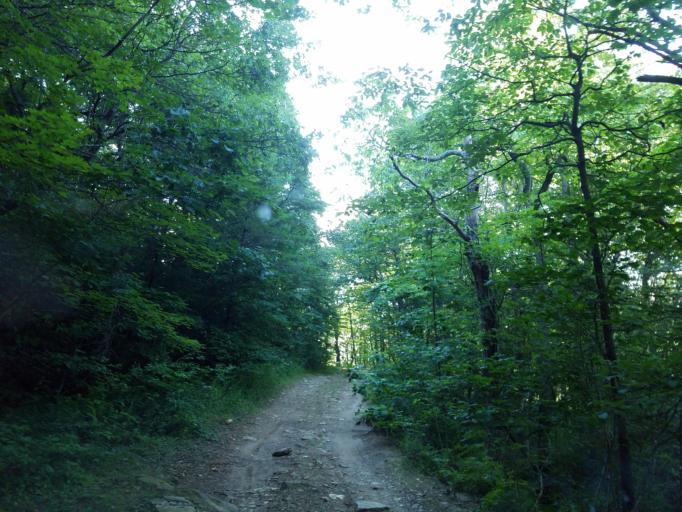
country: US
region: Georgia
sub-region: Dawson County
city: Dawsonville
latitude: 34.6095
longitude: -84.2202
